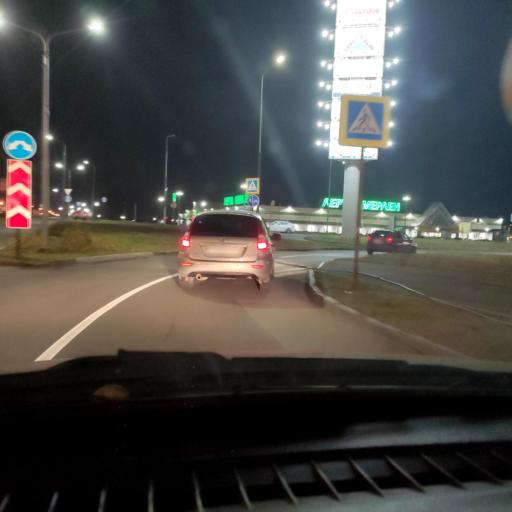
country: RU
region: Samara
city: Tol'yatti
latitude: 53.5489
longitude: 49.3426
